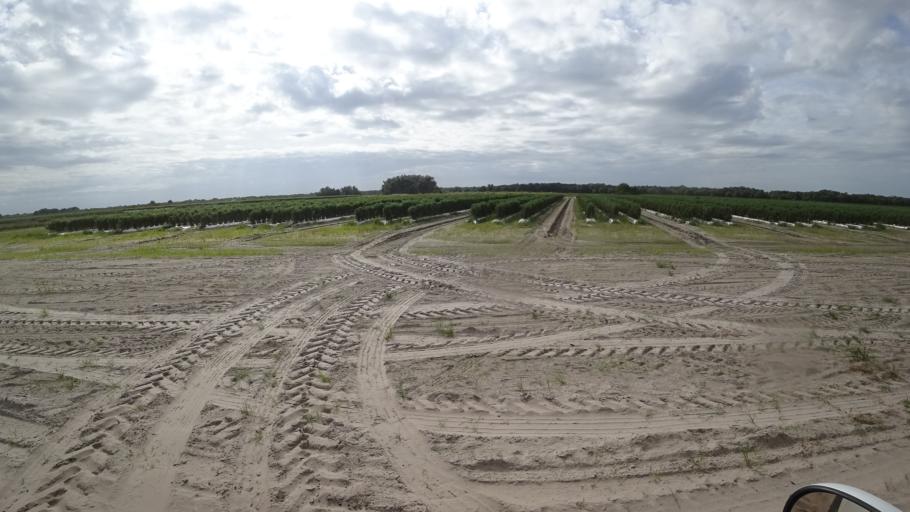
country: US
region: Florida
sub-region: Hillsborough County
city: Wimauma
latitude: 27.5831
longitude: -82.3147
